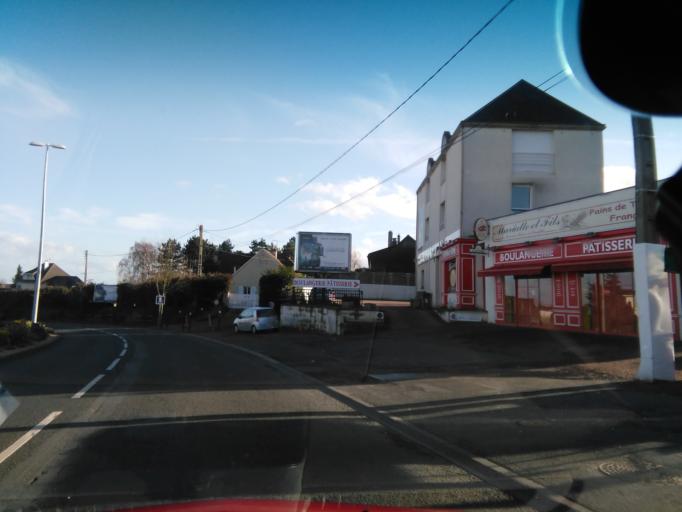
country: FR
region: Lower Normandy
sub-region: Departement du Calvados
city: Louvigny
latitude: 49.1726
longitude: -0.3893
